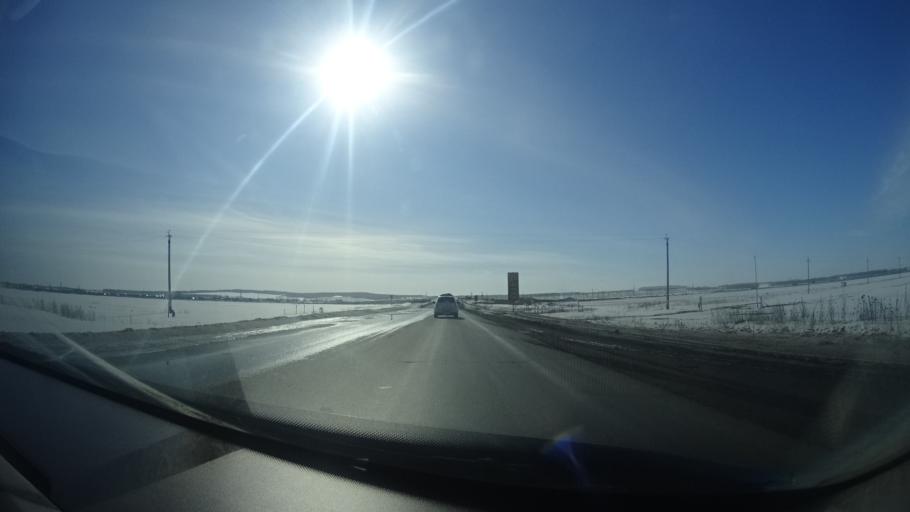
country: RU
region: Bashkortostan
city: Mikhaylovka
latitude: 54.8846
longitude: 55.7163
